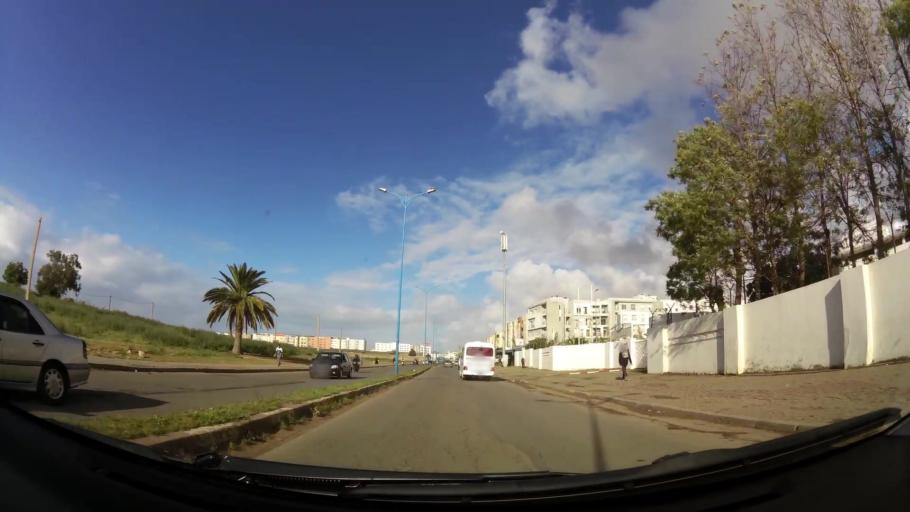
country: MA
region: Grand Casablanca
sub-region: Casablanca
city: Casablanca
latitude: 33.5509
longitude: -7.6966
